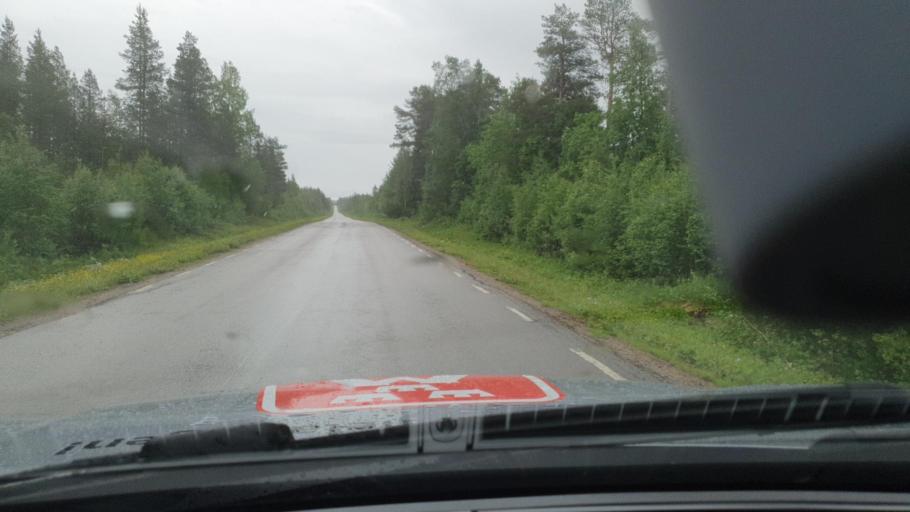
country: SE
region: Norrbotten
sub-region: Pajala Kommun
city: Pajala
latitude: 66.8392
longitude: 23.0837
